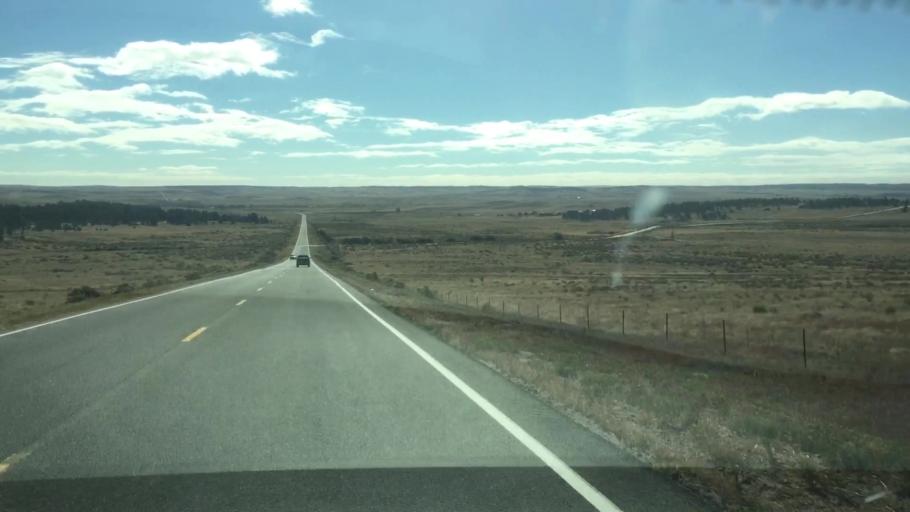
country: US
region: Colorado
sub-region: Elbert County
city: Kiowa
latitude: 39.3113
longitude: -104.3621
